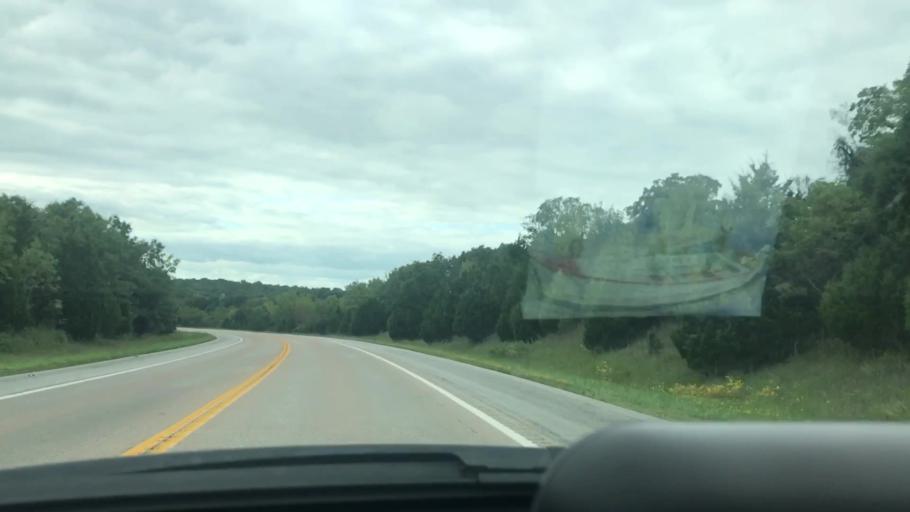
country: US
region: Missouri
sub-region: Benton County
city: Warsaw
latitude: 38.2043
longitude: -93.3266
